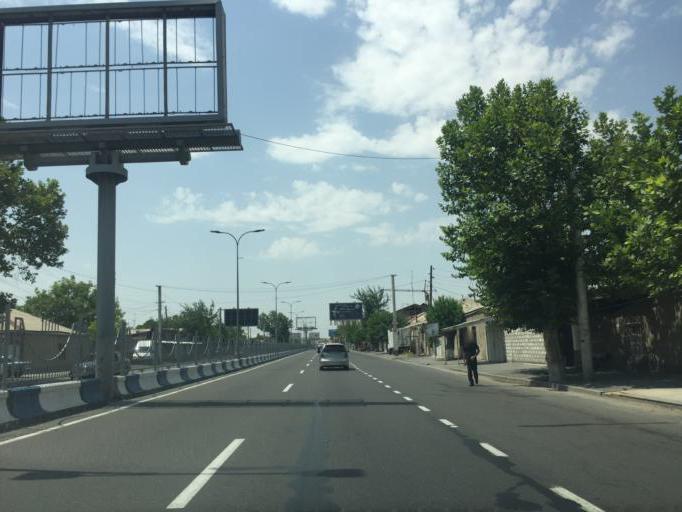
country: AM
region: Ararat
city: Argavand
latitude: 40.1623
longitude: 44.4221
